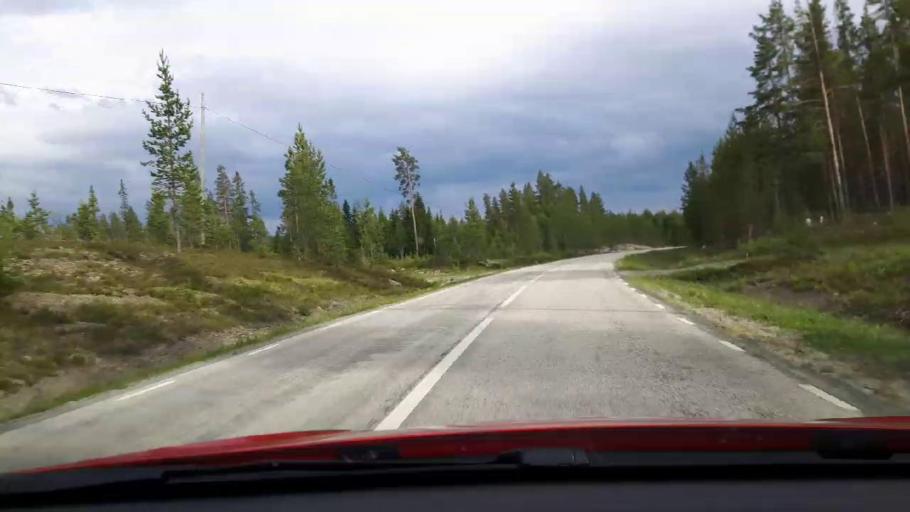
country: SE
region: Jaemtland
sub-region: Bergs Kommun
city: Hoverberg
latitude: 62.6607
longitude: 14.0547
